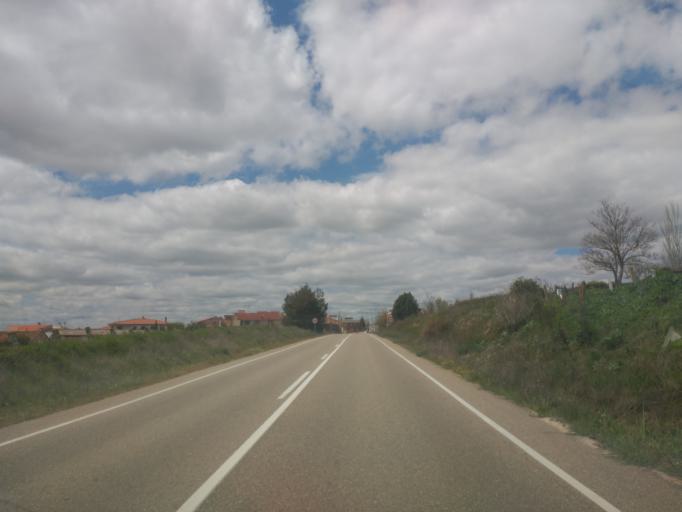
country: ES
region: Castille and Leon
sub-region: Provincia de Salamanca
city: Valverdon
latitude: 41.0460
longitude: -5.7658
